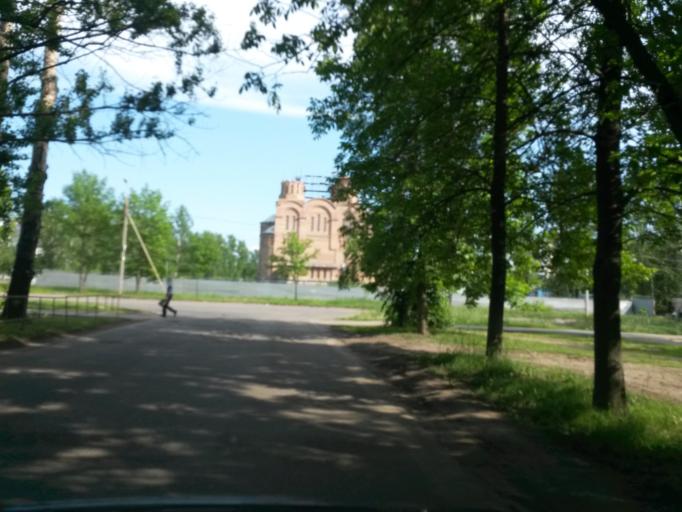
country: RU
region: Jaroslavl
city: Yaroslavl
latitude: 57.6908
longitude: 39.7745
